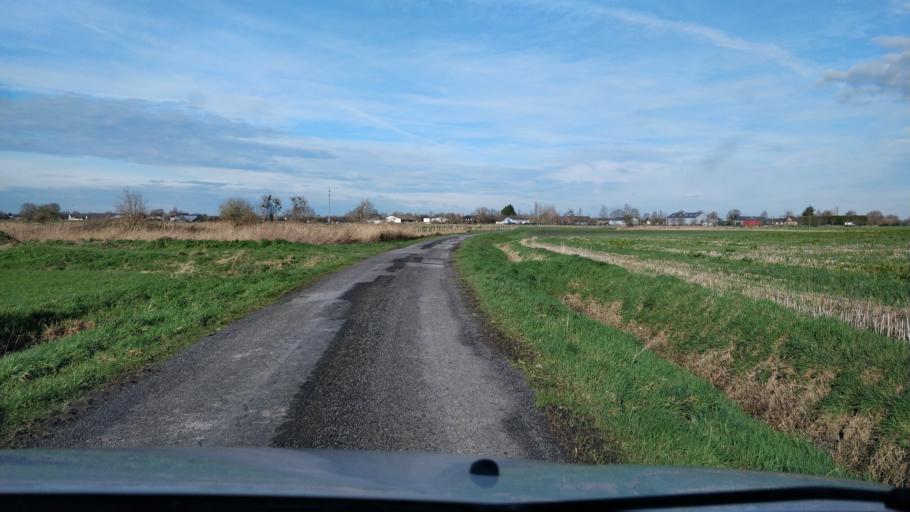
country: FR
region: Brittany
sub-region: Departement d'Ille-et-Vilaine
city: La Fresnais
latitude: 48.5781
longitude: -1.8294
